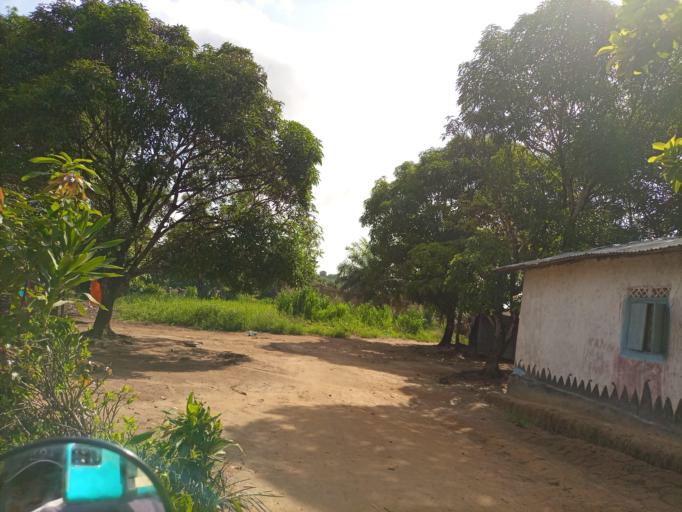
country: SL
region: Southern Province
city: Bo
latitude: 7.9667
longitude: -11.7647
